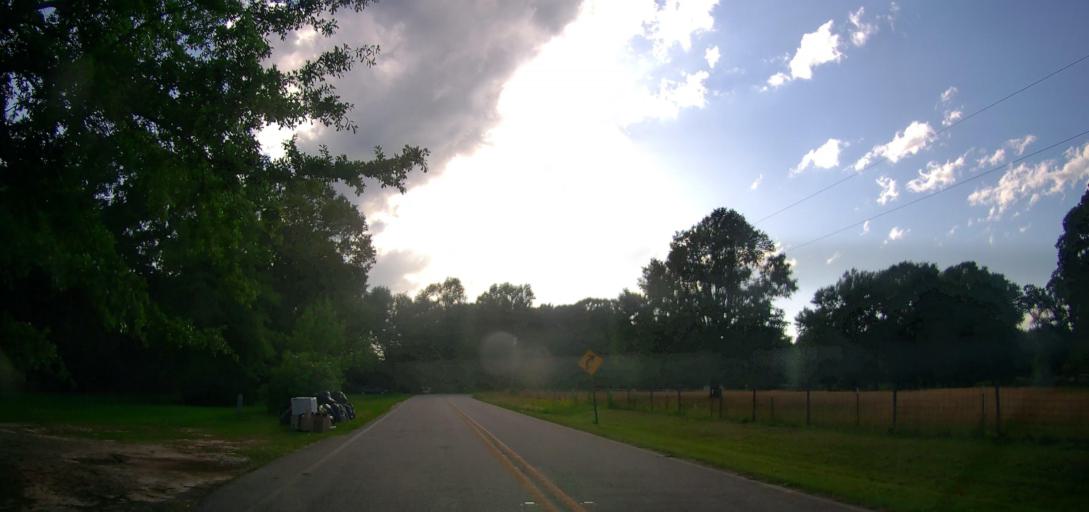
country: US
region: Georgia
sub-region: Peach County
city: Byron
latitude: 32.6555
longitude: -83.7900
